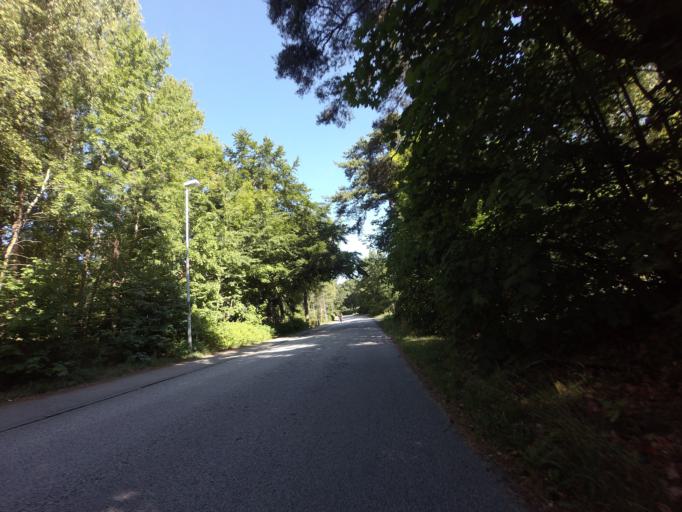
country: SE
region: Skane
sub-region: Ystads Kommun
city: Ystad
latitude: 55.4278
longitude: 13.8492
